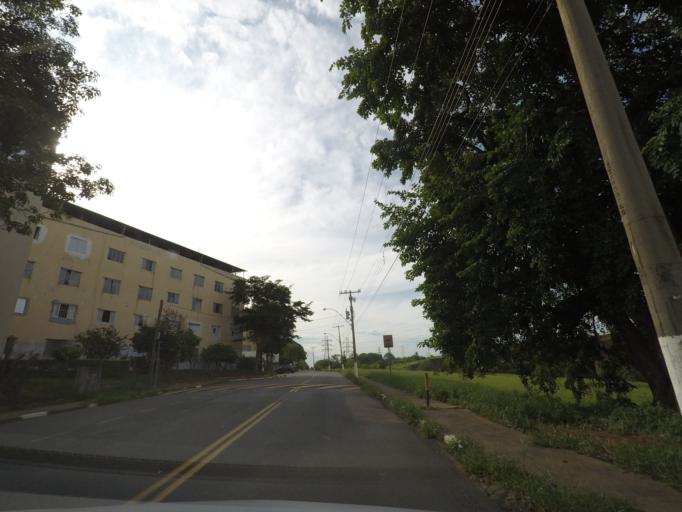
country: BR
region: Sao Paulo
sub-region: Campinas
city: Campinas
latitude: -22.9074
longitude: -47.1151
